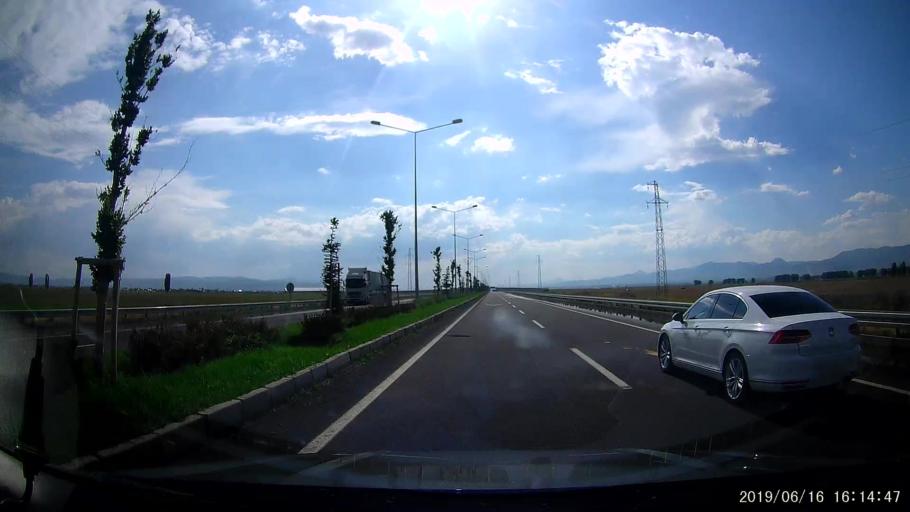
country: TR
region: Erzurum
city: Erzurum
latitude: 39.9612
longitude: 41.2402
